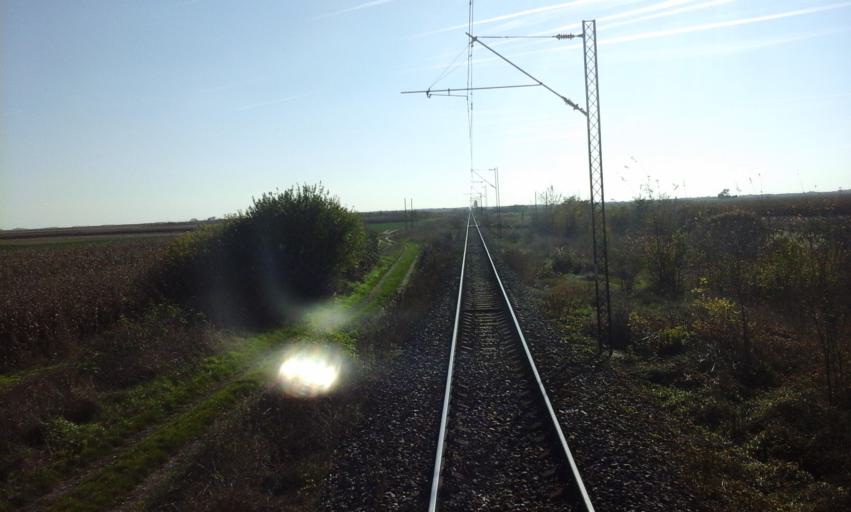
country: RS
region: Autonomna Pokrajina Vojvodina
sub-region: Severnobacki Okrug
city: Subotica
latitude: 45.9839
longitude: 19.6751
